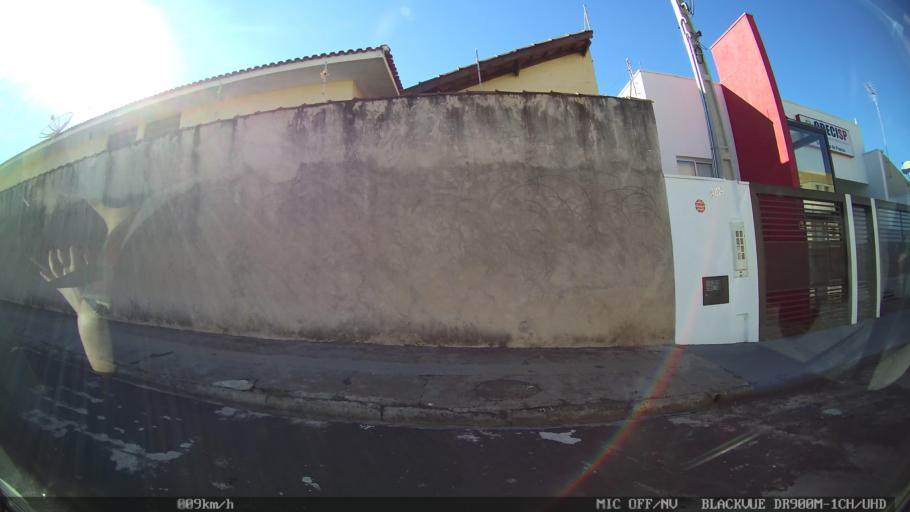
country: BR
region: Sao Paulo
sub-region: Franca
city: Franca
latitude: -20.5489
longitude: -47.4073
